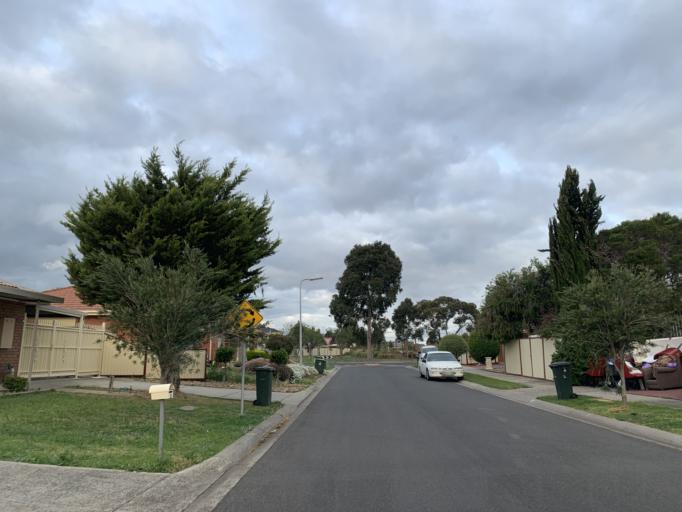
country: AU
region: Victoria
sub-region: Brimbank
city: Kealba
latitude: -37.7494
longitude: 144.8253
